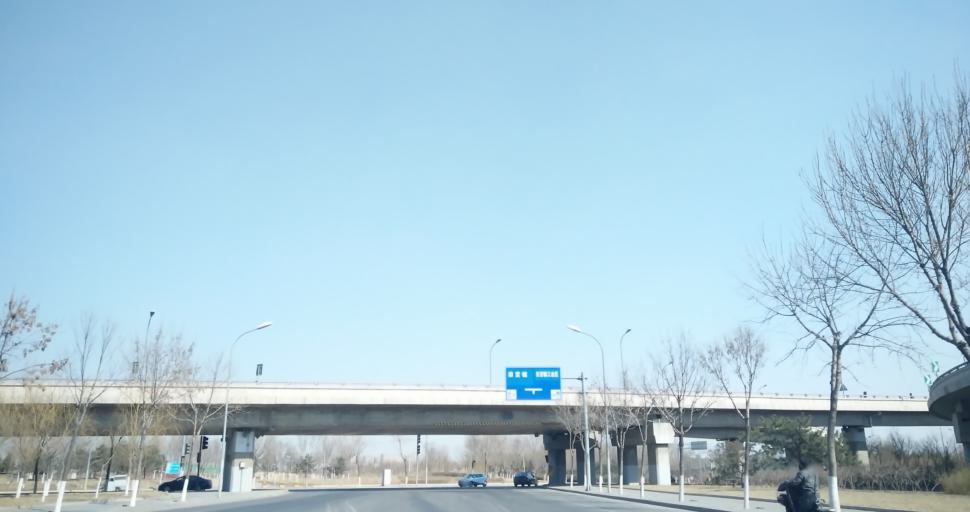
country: CN
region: Beijing
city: Yinghai
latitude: 39.7875
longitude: 116.4248
